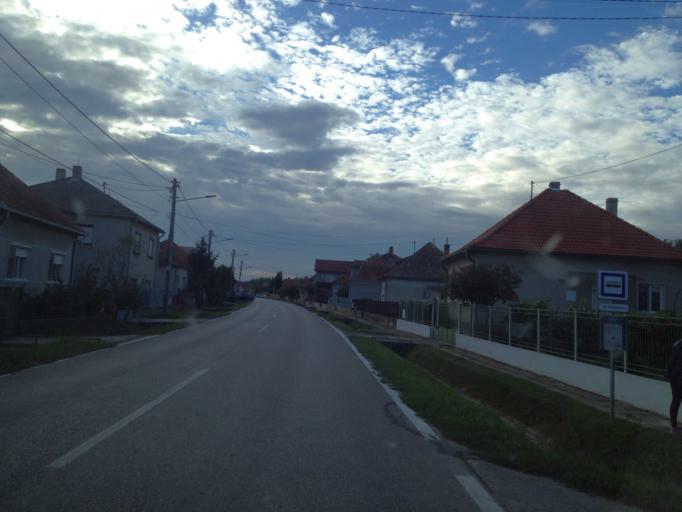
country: HU
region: Komarom-Esztergom
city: Almasfuzito
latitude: 47.7541
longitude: 18.2165
